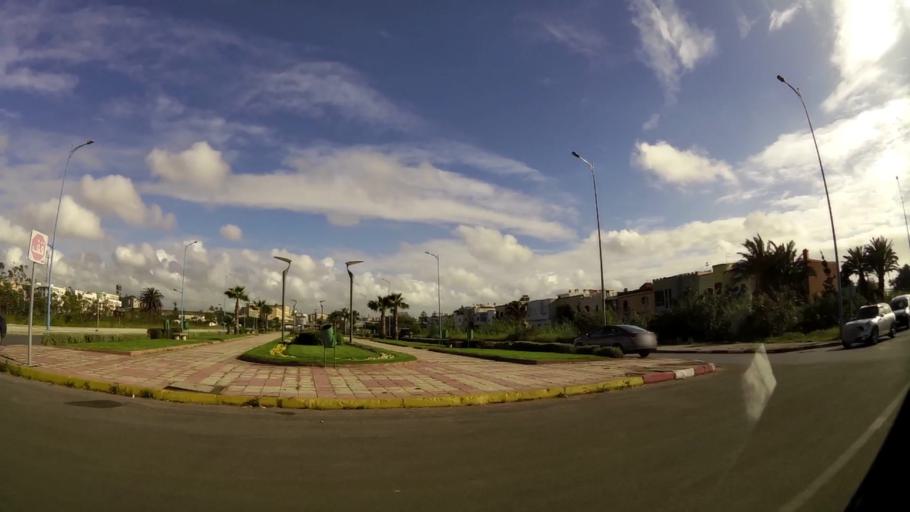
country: MA
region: Grand Casablanca
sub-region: Mohammedia
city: Mohammedia
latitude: 33.7053
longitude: -7.3732
